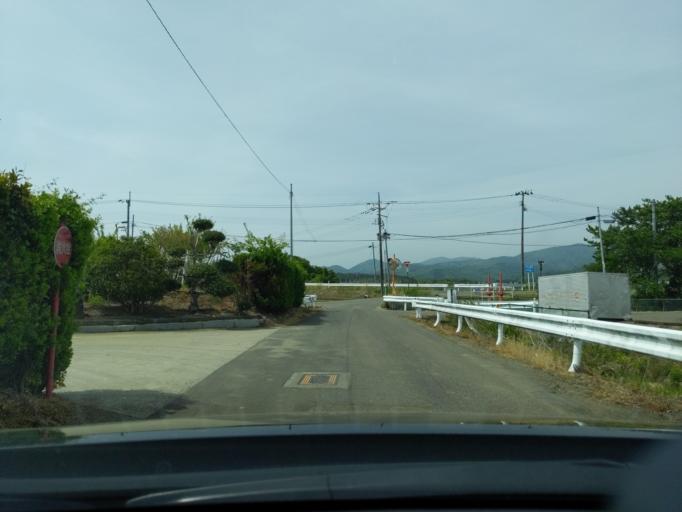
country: JP
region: Fukushima
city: Koriyama
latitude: 37.4002
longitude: 140.2905
